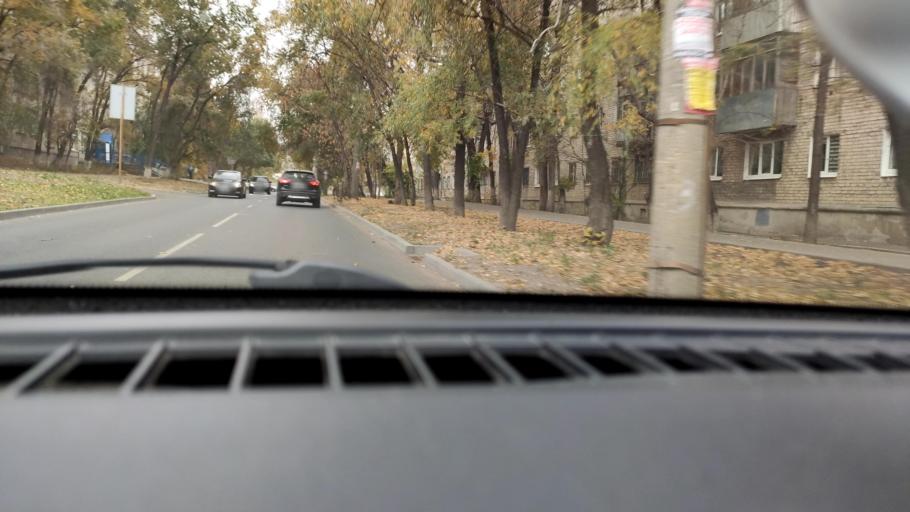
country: RU
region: Samara
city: Samara
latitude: 53.2106
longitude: 50.2207
